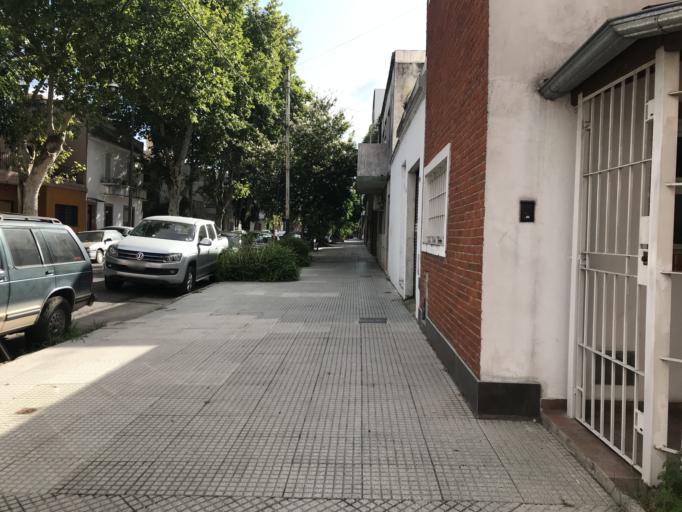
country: AR
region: Buenos Aires F.D.
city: Villa Santa Rita
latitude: -34.6317
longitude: -58.4477
